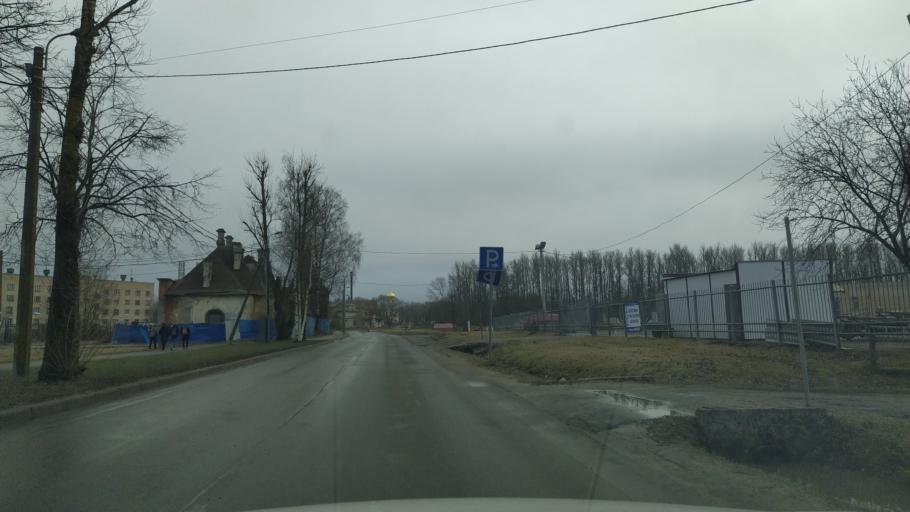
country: RU
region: St.-Petersburg
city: Pushkin
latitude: 59.7319
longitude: 30.3829
